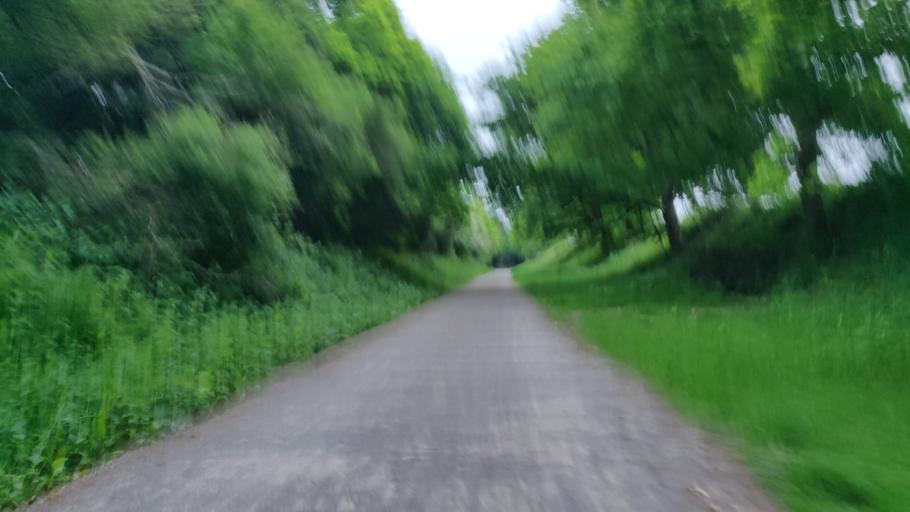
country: GB
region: England
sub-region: West Sussex
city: Partridge Green
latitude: 50.9695
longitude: -0.3153
